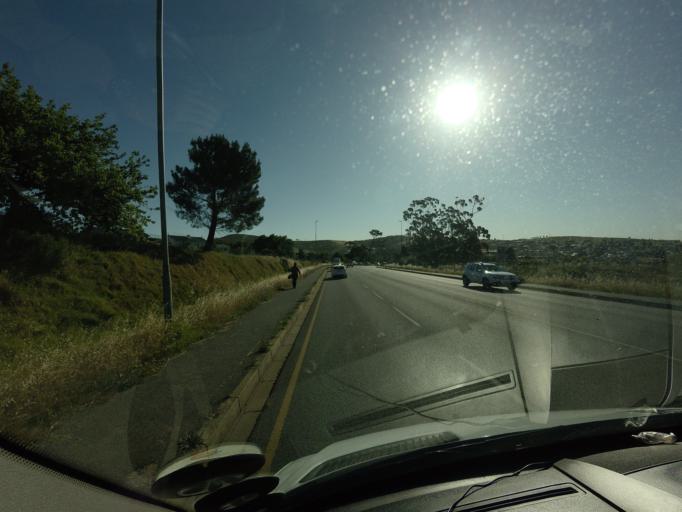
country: ZA
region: Western Cape
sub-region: Cape Winelands District Municipality
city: Stellenbosch
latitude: -33.9224
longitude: 18.8597
